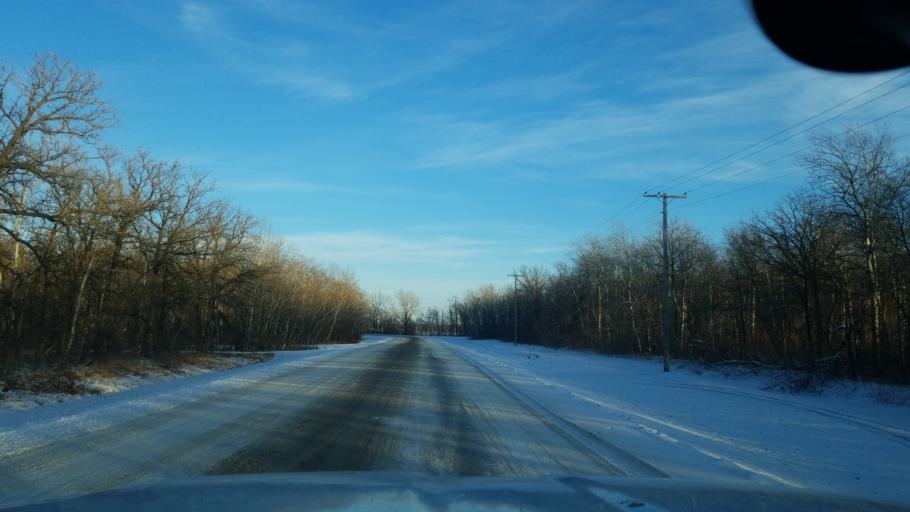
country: CA
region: Manitoba
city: Portage la Prairie
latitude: 49.9455
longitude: -98.3446
